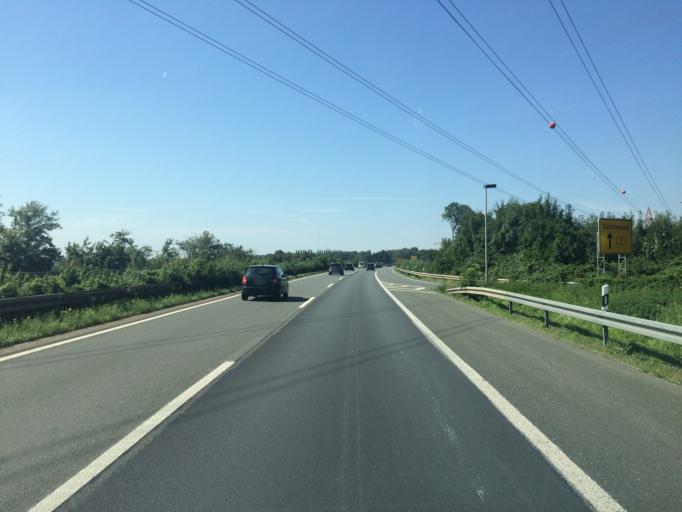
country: DE
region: North Rhine-Westphalia
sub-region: Regierungsbezirk Arnsberg
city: Holzwickede
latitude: 51.5061
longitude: 7.5918
